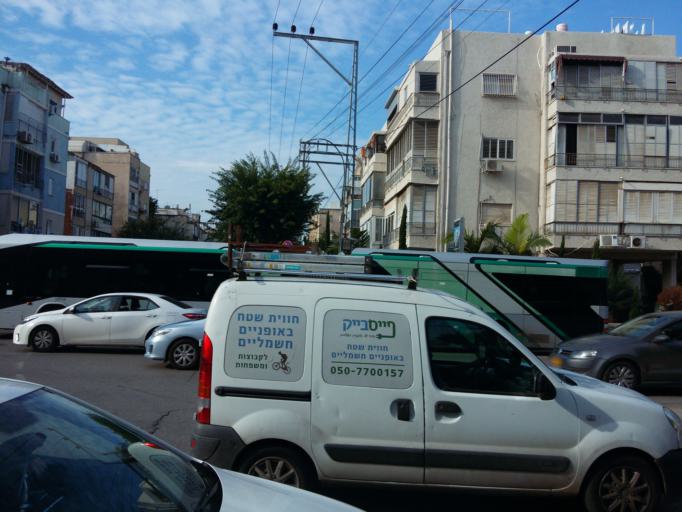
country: IL
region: Tel Aviv
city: Tel Aviv
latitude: 32.0938
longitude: 34.7946
